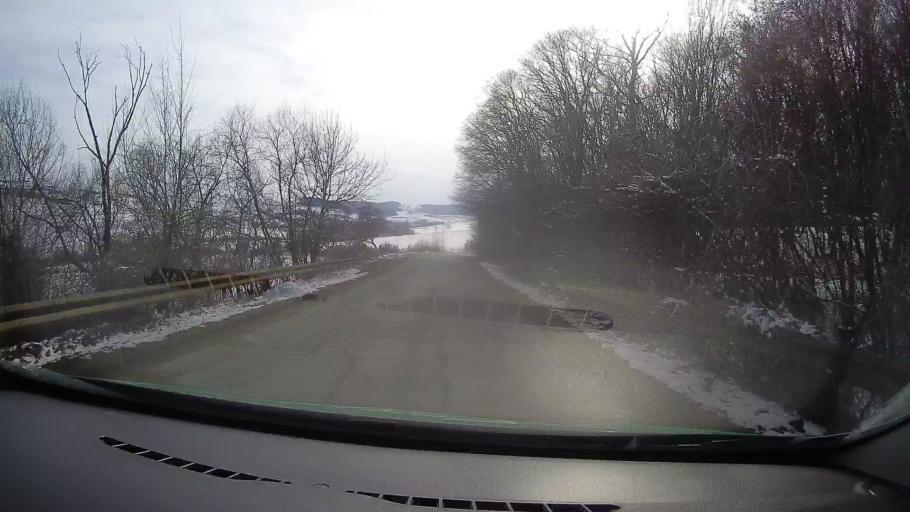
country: RO
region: Sibiu
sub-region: Comuna Bradeni
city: Bradeni
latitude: 46.0979
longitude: 24.8364
